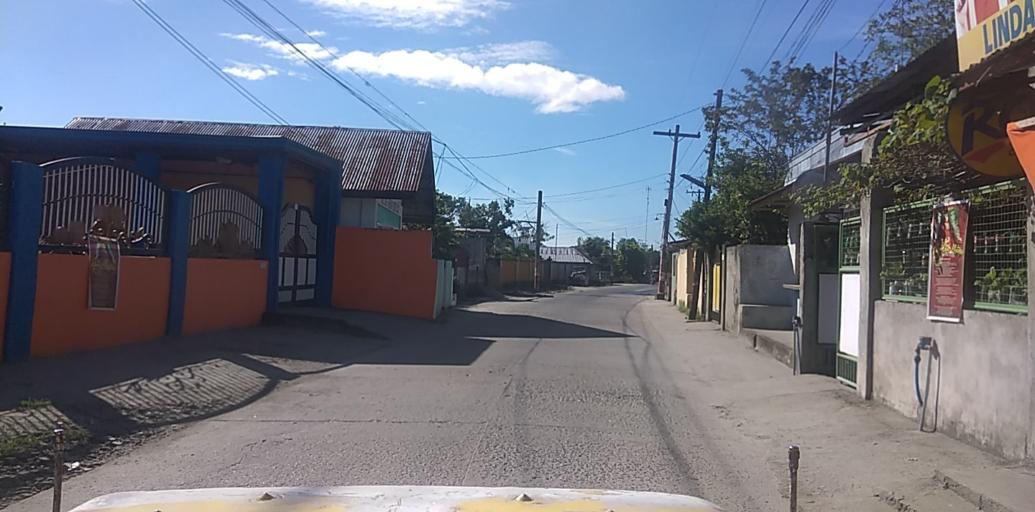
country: PH
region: Central Luzon
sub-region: Province of Pampanga
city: San Patricio
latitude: 15.0975
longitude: 120.7139
